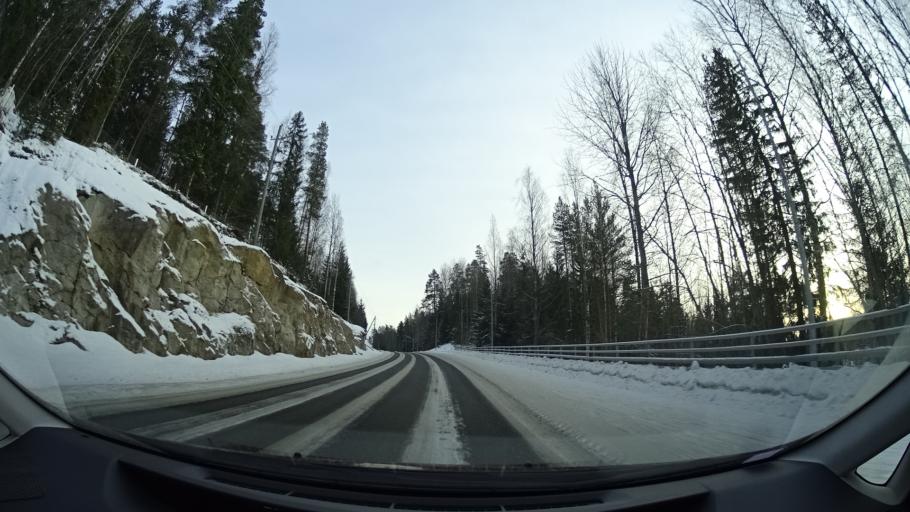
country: FI
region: Uusimaa
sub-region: Helsinki
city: Espoo
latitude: 60.2739
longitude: 24.5928
